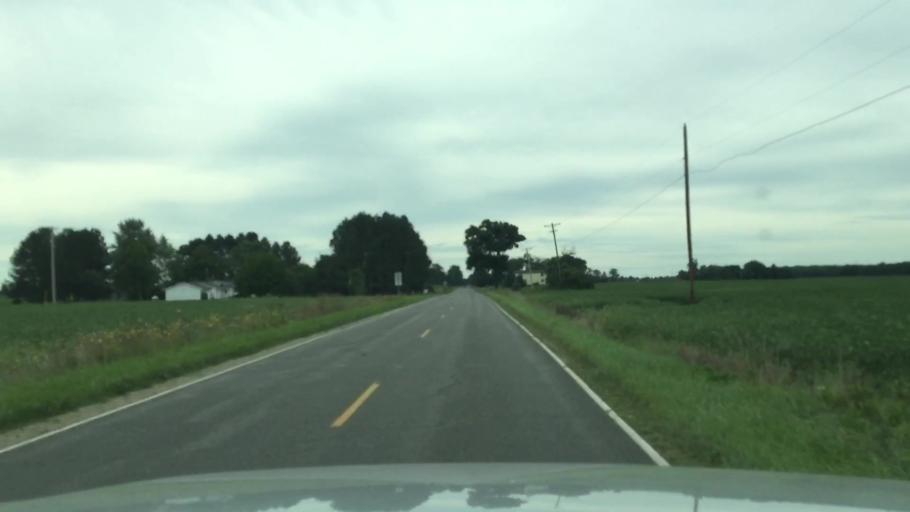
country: US
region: Michigan
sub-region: Shiawassee County
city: Durand
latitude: 43.0295
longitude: -83.9872
